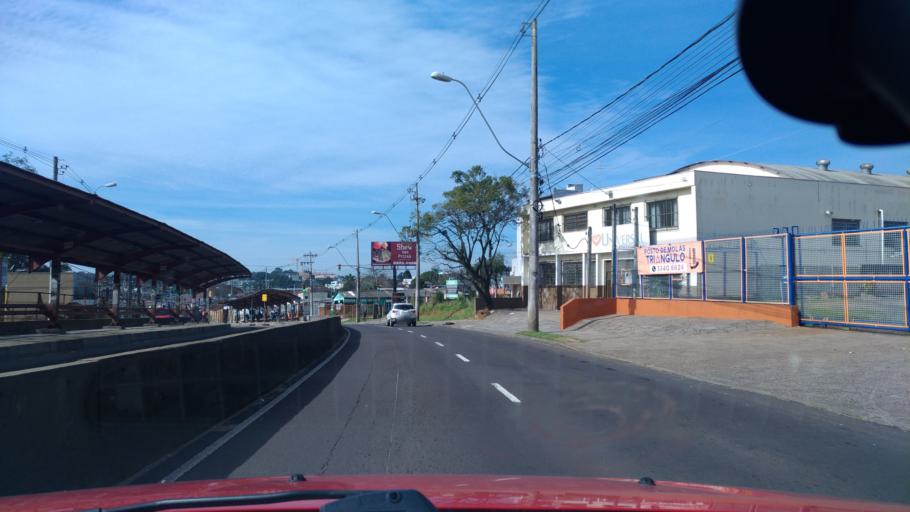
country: BR
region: Rio Grande do Sul
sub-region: Cachoeirinha
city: Cachoeirinha
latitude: -30.0114
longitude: -51.1305
